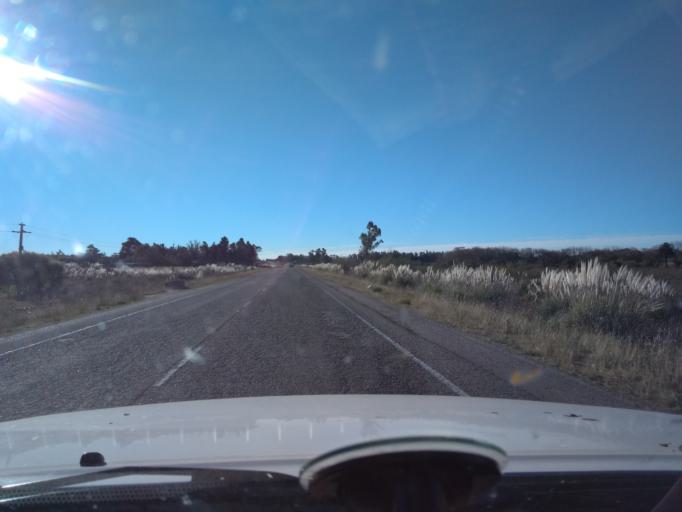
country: UY
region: Canelones
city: Sauce
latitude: -34.6005
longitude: -56.0501
